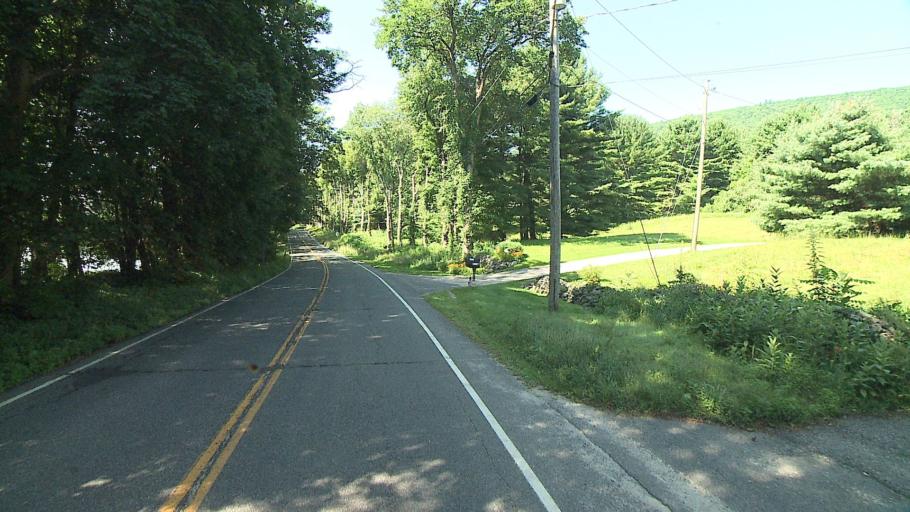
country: US
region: Connecticut
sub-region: Litchfield County
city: Canaan
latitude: 42.0389
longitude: -73.4254
